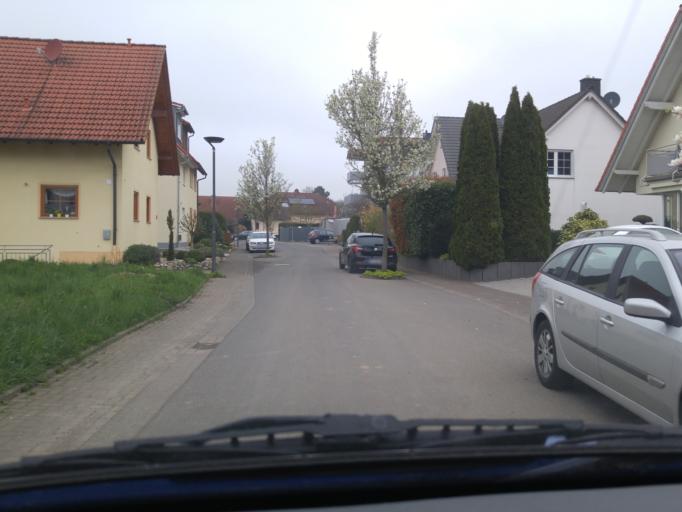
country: DE
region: Hesse
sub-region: Regierungsbezirk Darmstadt
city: Friedberg
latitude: 50.2982
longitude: 8.7566
